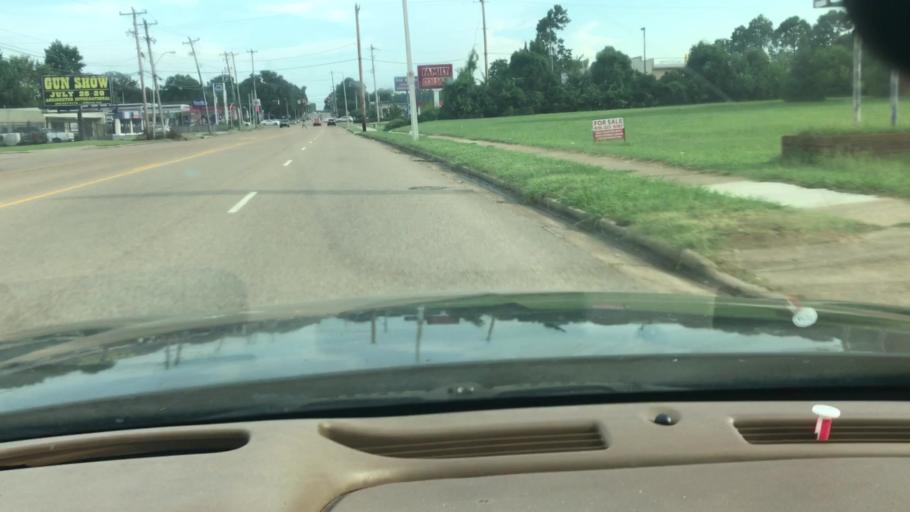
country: US
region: Tennessee
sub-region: Shelby County
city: New South Memphis
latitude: 35.0560
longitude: -90.0075
